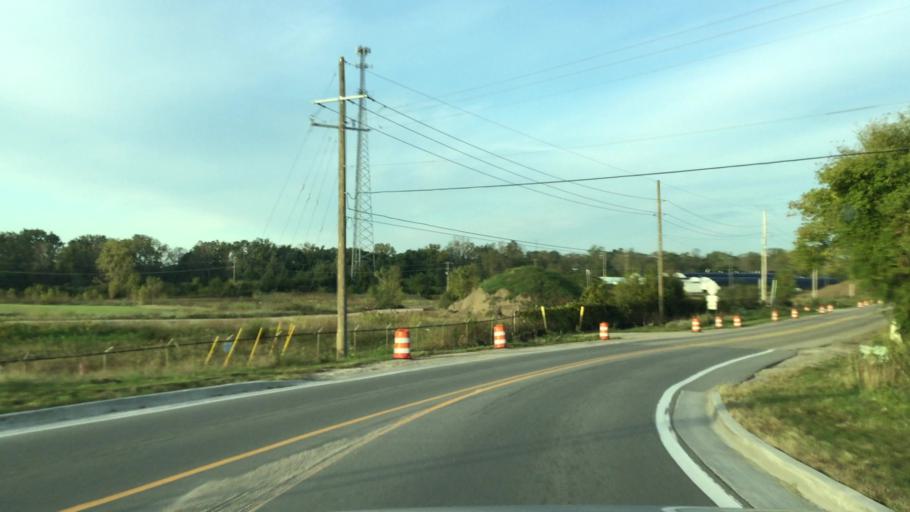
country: US
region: Michigan
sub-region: Livingston County
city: Whitmore Lake
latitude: 42.4292
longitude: -83.7696
